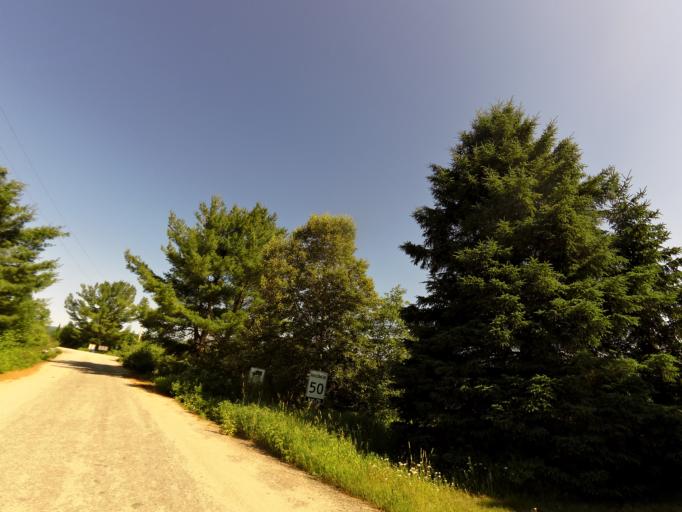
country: CA
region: Ontario
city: Mattawa
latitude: 46.2523
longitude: -78.2872
